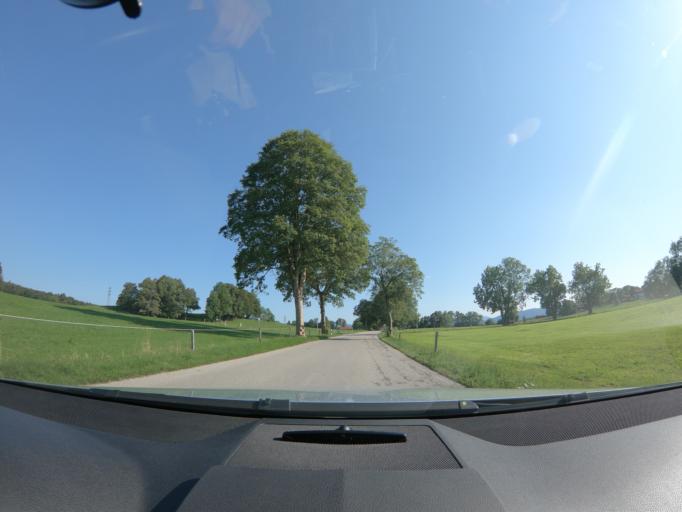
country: DE
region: Bavaria
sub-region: Upper Bavaria
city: Warngau
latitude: 47.8181
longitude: 11.7239
